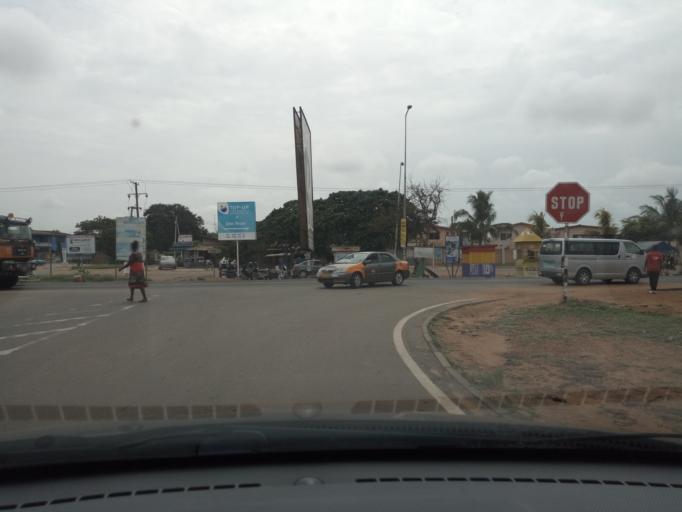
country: GH
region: Greater Accra
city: Tema
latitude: 5.6754
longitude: -0.0218
